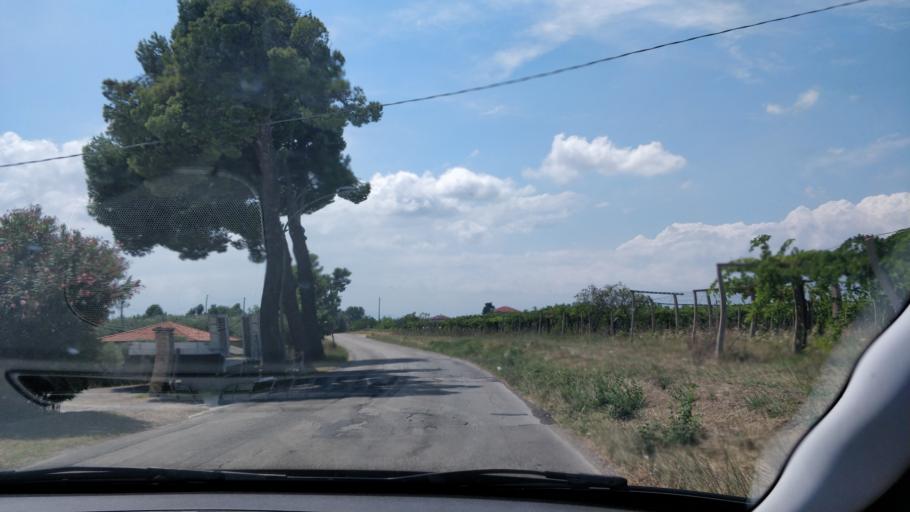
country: IT
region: Abruzzo
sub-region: Provincia di Chieti
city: Torrevecchia
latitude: 42.4148
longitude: 14.2284
